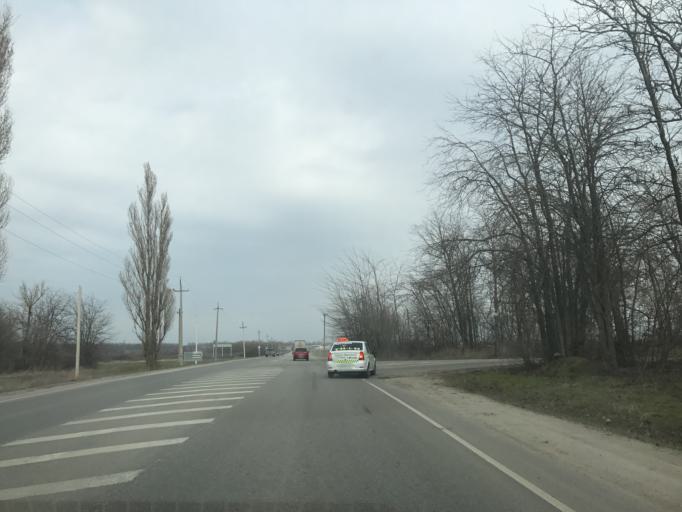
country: RU
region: Rostov
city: Aksay
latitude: 47.3127
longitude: 39.9546
